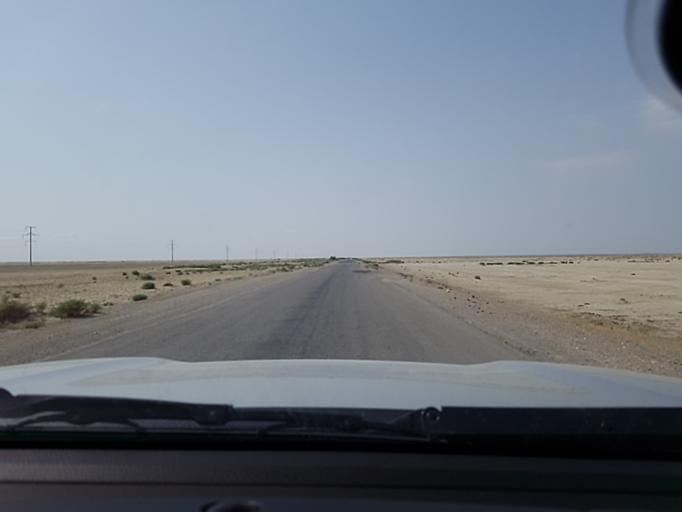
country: TM
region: Balkan
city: Gumdag
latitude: 38.9863
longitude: 54.5870
